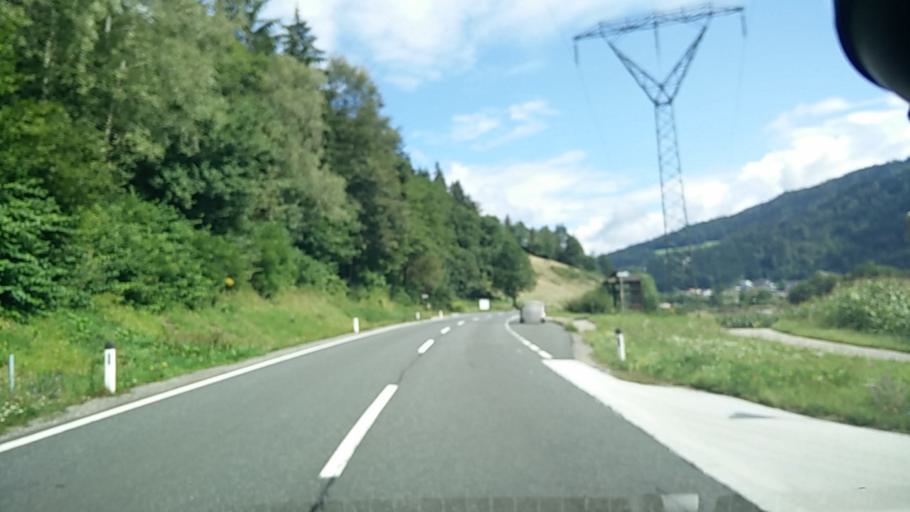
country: AT
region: Carinthia
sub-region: Politischer Bezirk Sankt Veit an der Glan
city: Bruckl
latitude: 46.7387
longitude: 14.5281
